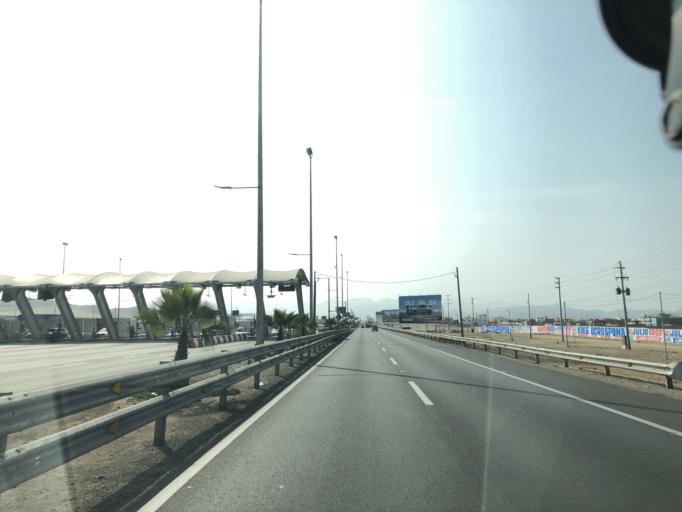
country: PE
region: Lima
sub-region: Lima
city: San Bartolo
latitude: -12.3661
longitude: -76.7902
